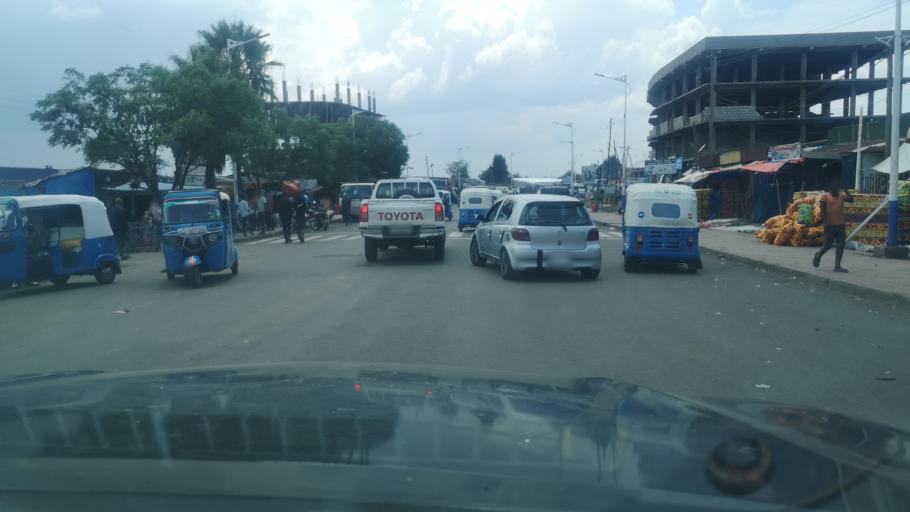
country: ET
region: Oromiya
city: Waliso
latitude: 8.2838
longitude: 37.7798
